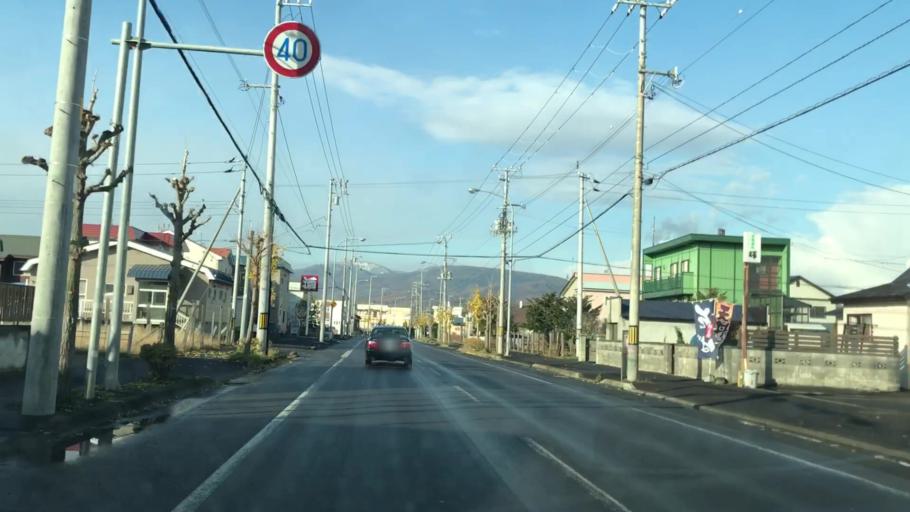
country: JP
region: Hokkaido
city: Yoichi
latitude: 43.1829
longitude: 140.8017
